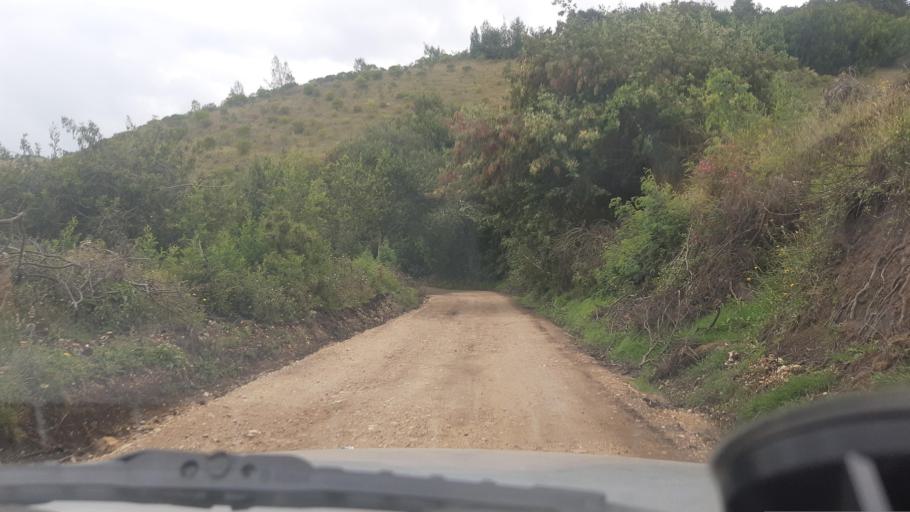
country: CO
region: Cundinamarca
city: Suesca
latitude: 5.1481
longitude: -73.7927
